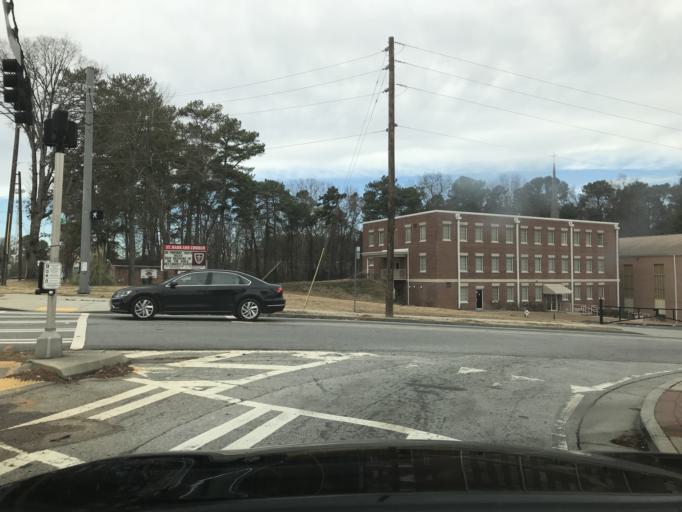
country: US
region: Georgia
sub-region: Fulton County
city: East Point
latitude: 33.6903
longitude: -84.5061
